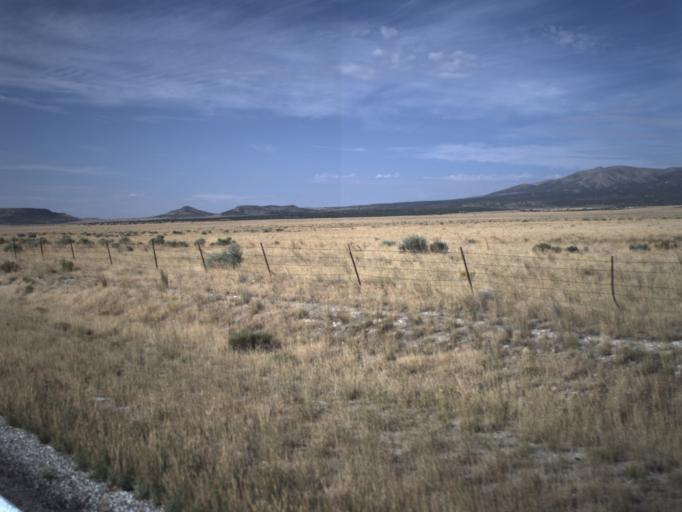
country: US
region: Idaho
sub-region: Oneida County
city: Malad City
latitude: 41.9041
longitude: -113.1045
